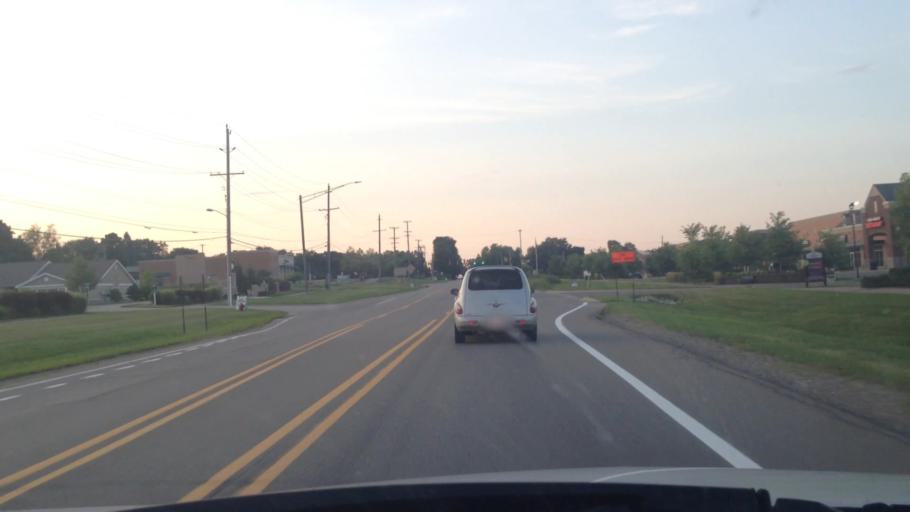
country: US
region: Michigan
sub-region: Oakland County
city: Auburn Hills
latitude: 42.7259
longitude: -83.3076
